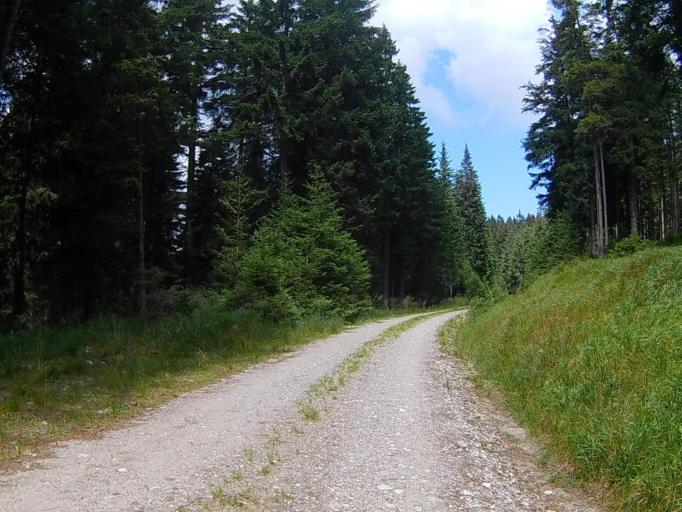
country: SI
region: Lovrenc na Pohorju
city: Lovrenc na Pohorju
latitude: 46.4808
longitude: 15.4022
